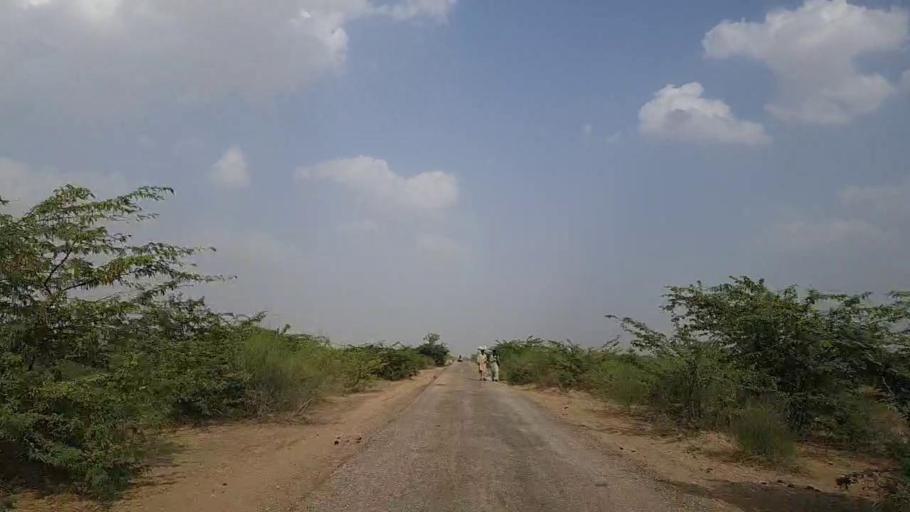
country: PK
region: Sindh
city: Islamkot
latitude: 24.8679
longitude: 70.1149
